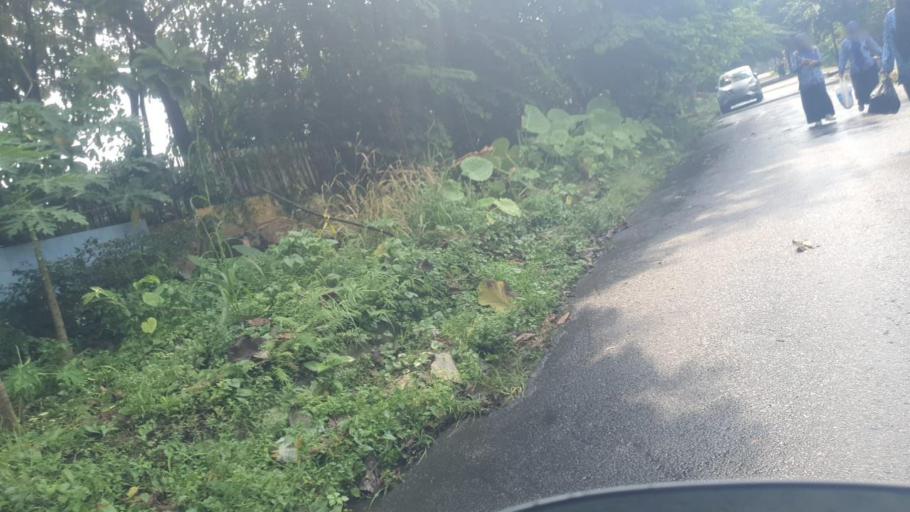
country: ID
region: West Java
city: Bogor
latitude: -6.5867
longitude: 106.8044
